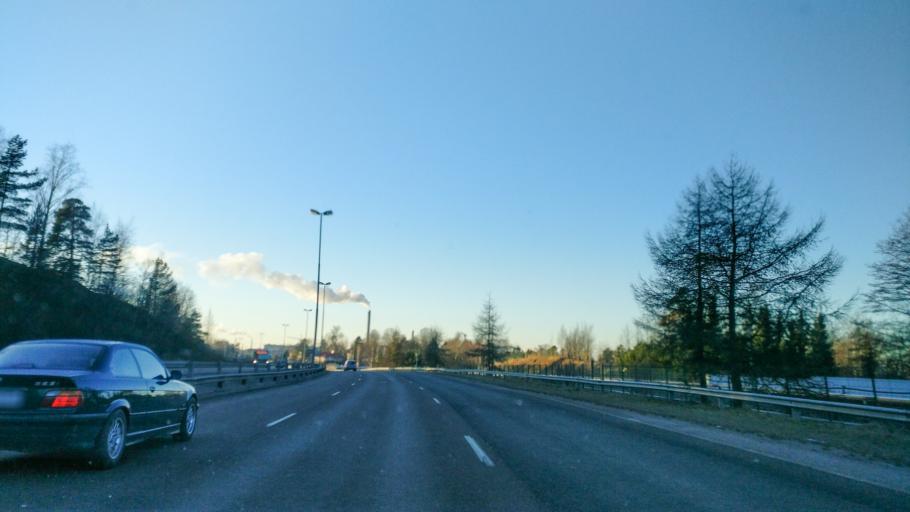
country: FI
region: Uusimaa
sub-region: Helsinki
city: Helsinki
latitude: 60.1885
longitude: 25.0068
